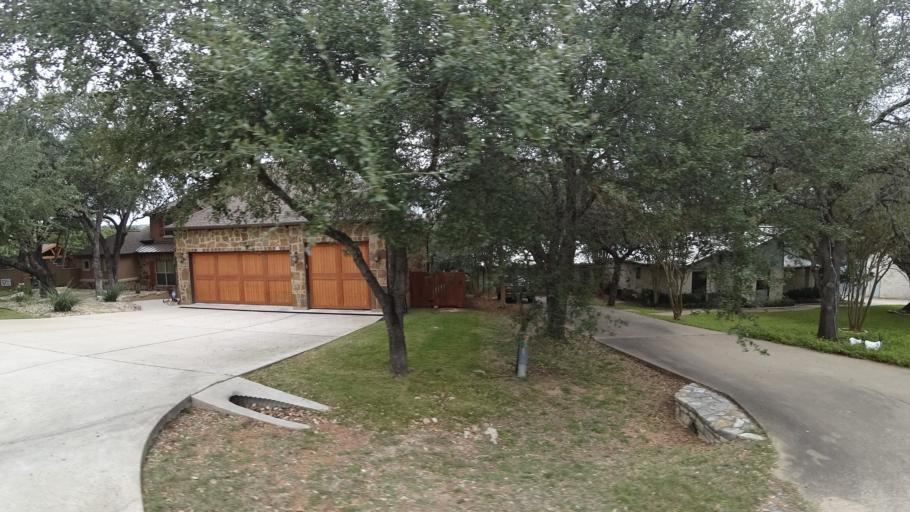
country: US
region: Texas
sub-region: Travis County
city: Bee Cave
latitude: 30.3313
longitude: -97.9214
